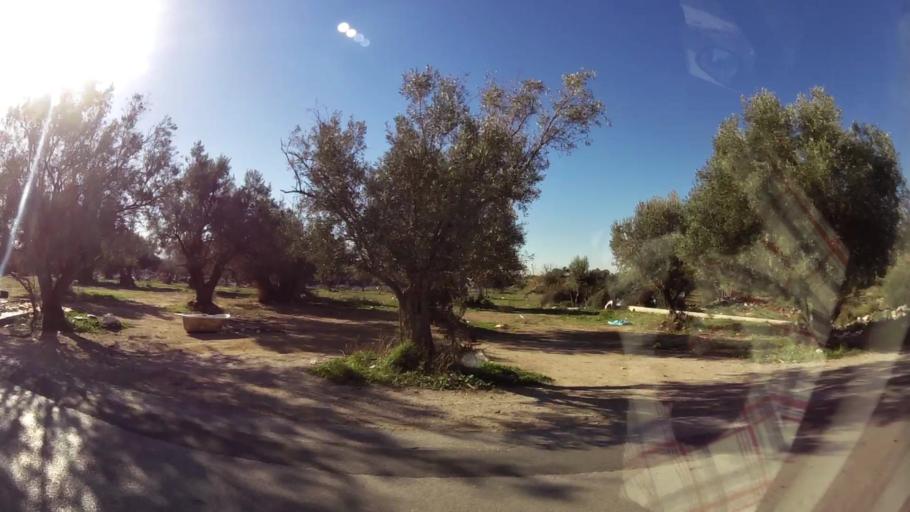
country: GR
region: Attica
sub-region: Nomarchia Athinas
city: Metamorfosi
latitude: 38.0791
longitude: 23.7548
